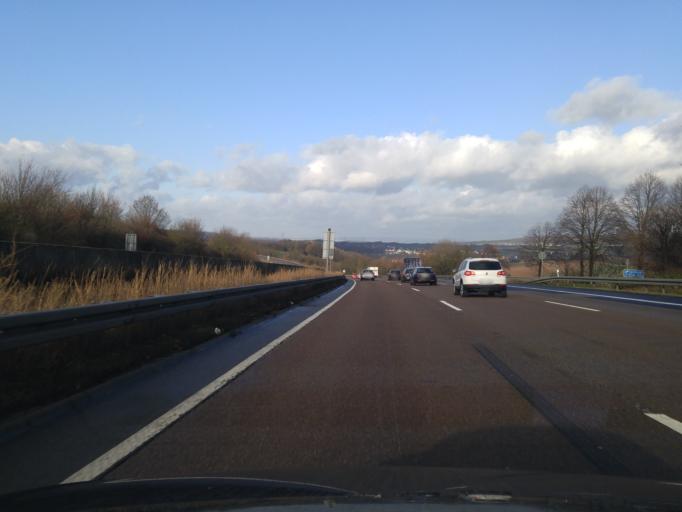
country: DE
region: Hesse
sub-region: Regierungsbezirk Kassel
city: Guxhagen
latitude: 51.1811
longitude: 9.4738
